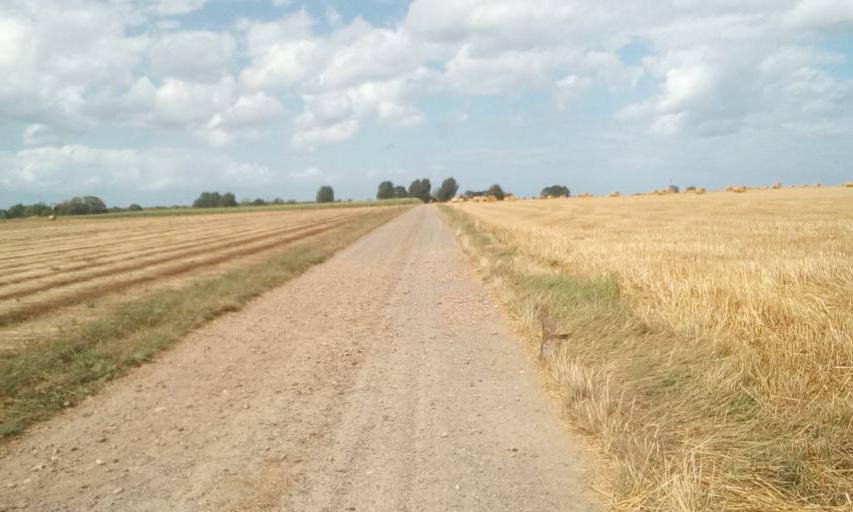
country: FR
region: Lower Normandy
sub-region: Departement du Calvados
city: Ver-sur-Mer
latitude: 49.3233
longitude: -0.5280
